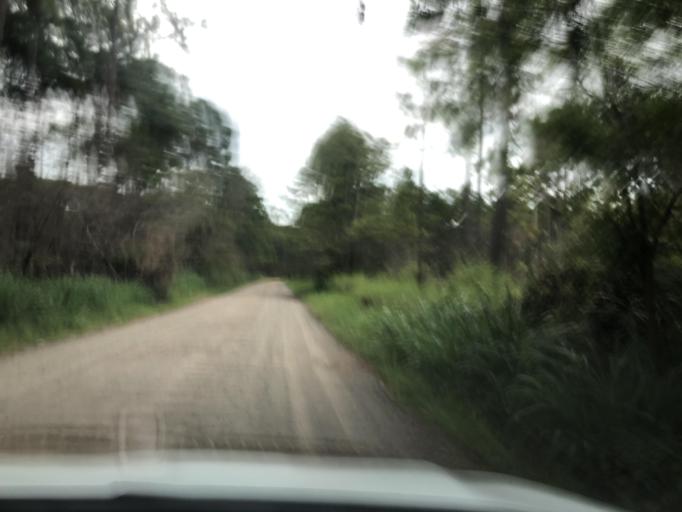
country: BR
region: Santa Catarina
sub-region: Florianopolis
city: Lagoa
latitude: -27.5484
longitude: -48.4418
